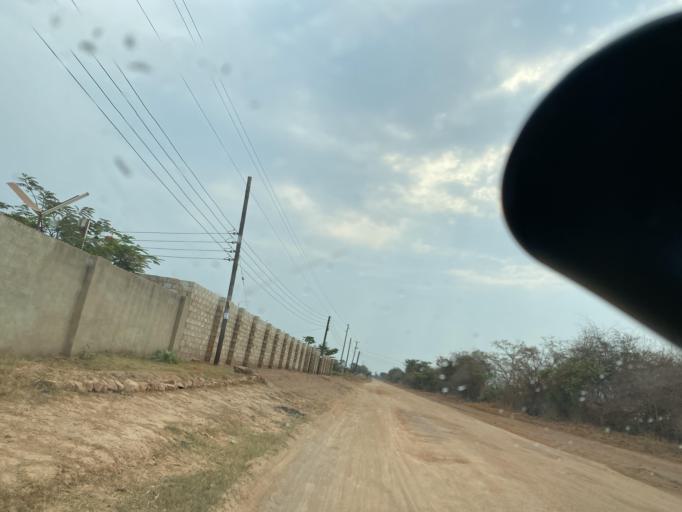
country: ZM
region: Lusaka
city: Lusaka
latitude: -15.2888
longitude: 28.2850
